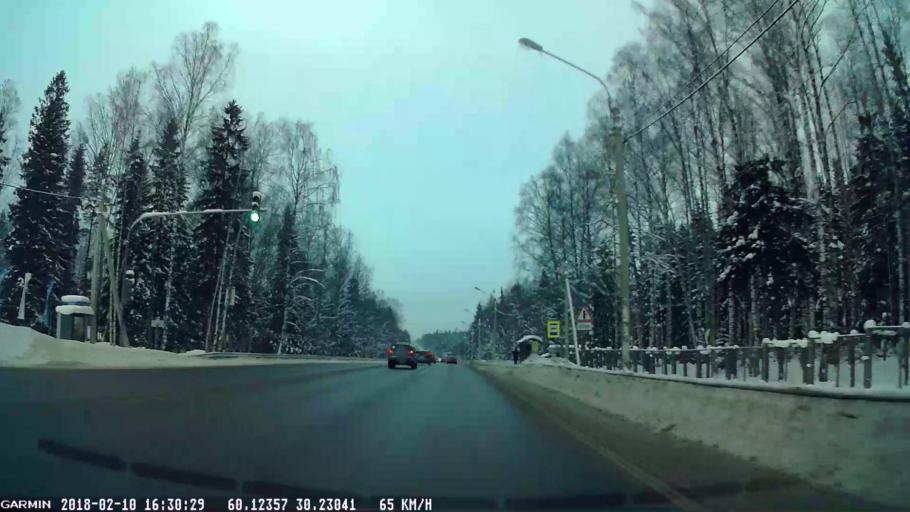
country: RU
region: St.-Petersburg
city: Levashovo
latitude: 60.1242
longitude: 30.2297
